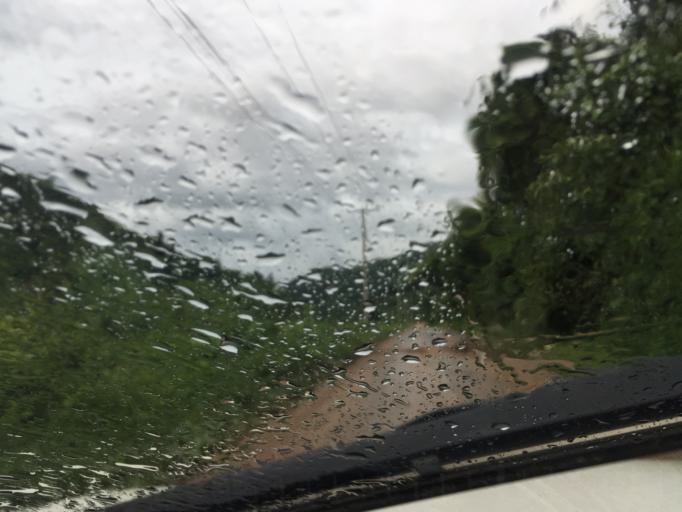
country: LA
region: Oudomxai
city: Muang La
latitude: 21.0251
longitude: 102.2342
